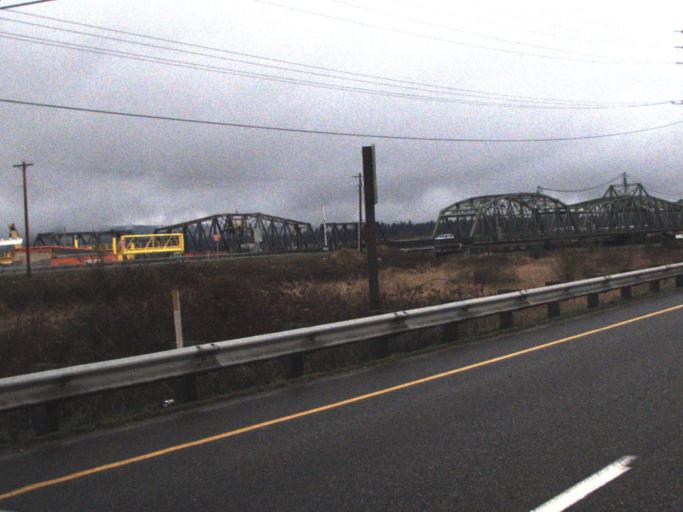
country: US
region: Washington
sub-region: Snohomish County
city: Marysville
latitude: 48.0337
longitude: -122.1818
